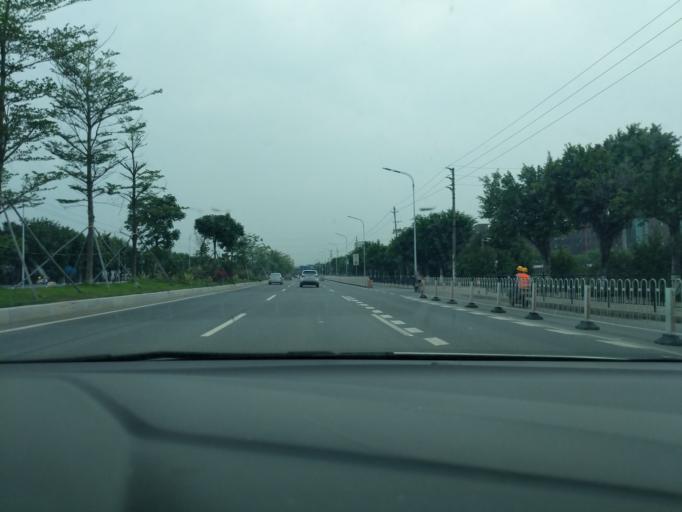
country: CN
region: Guangdong
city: Dongyong
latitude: 22.8614
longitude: 113.4843
